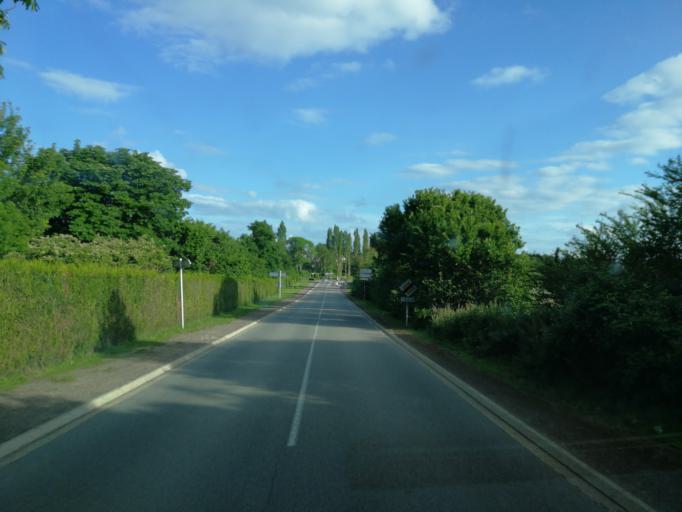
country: FR
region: Haute-Normandie
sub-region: Departement de l'Eure
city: Damville
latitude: 48.8713
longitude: 1.0685
